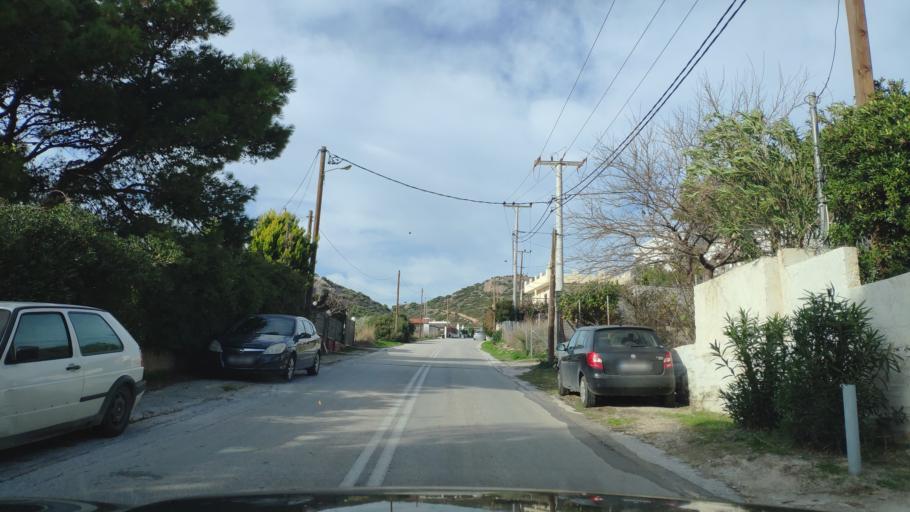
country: GR
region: Attica
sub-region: Nomarchia Anatolikis Attikis
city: Limin Mesoyaias
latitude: 37.9003
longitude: 24.0233
